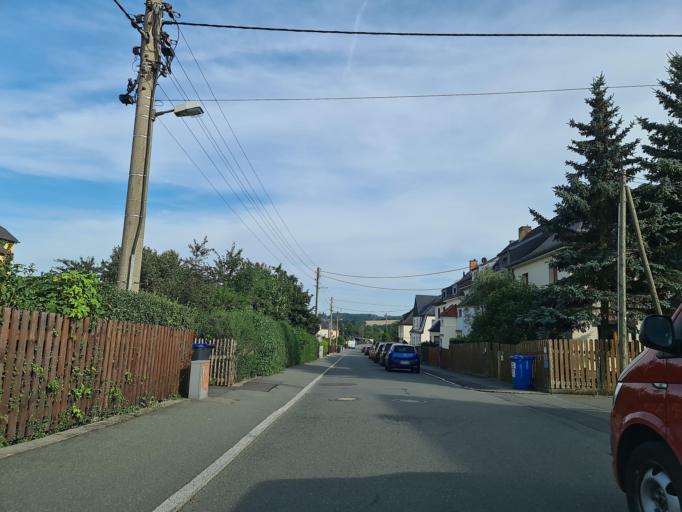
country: DE
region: Saxony
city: Plauen
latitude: 50.4883
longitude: 12.1003
